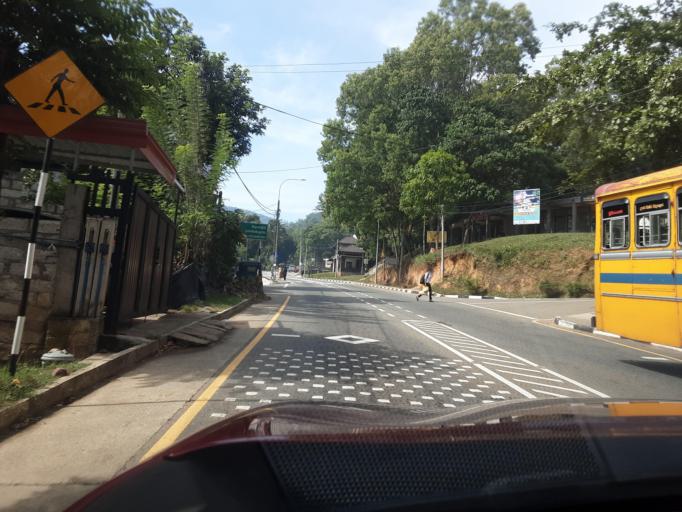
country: LK
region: Uva
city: Badulla
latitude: 6.9843
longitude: 81.0790
